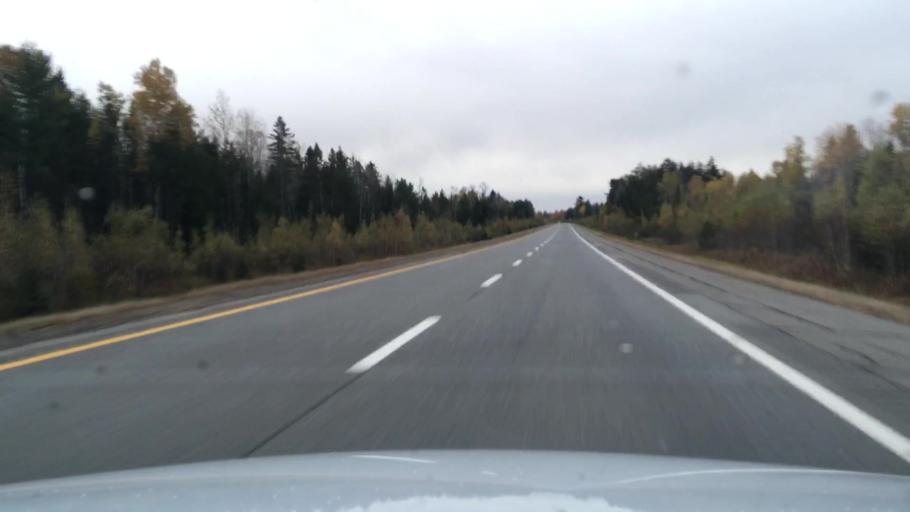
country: US
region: Maine
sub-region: Penobscot County
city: Greenbush
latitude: 45.1087
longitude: -68.6956
